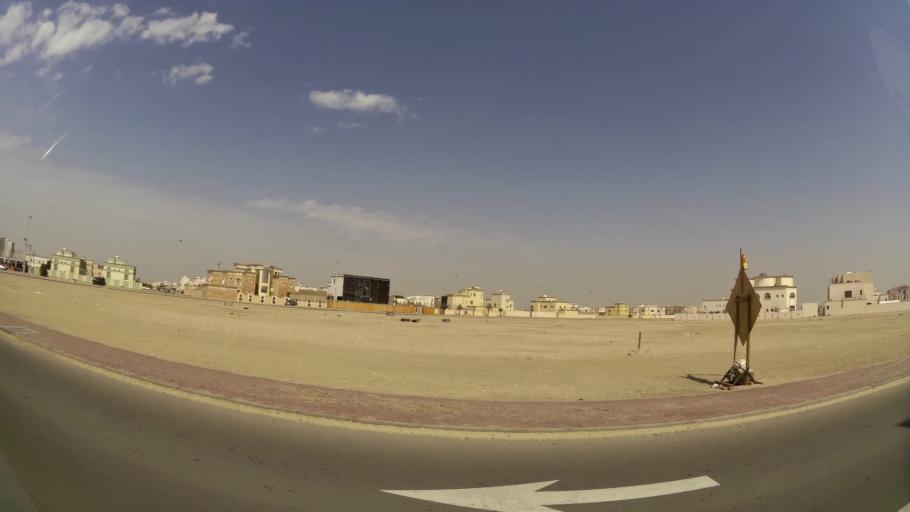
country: AE
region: Abu Dhabi
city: Abu Dhabi
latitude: 24.3141
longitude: 54.5410
